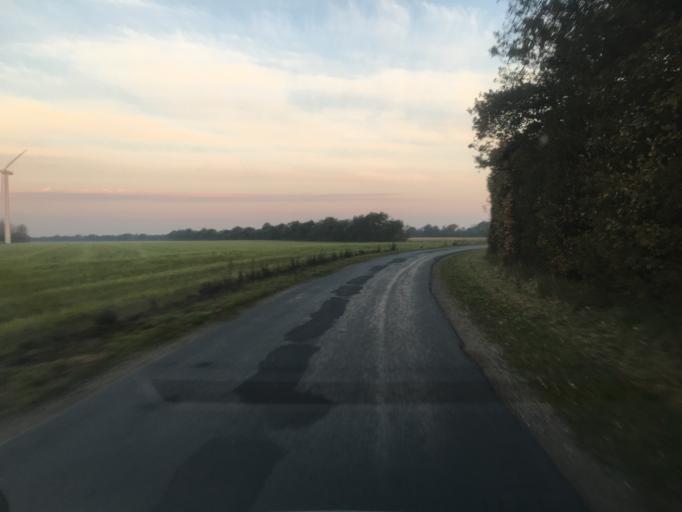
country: DK
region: South Denmark
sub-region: Tonder Kommune
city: Logumkloster
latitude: 54.9871
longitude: 9.0527
